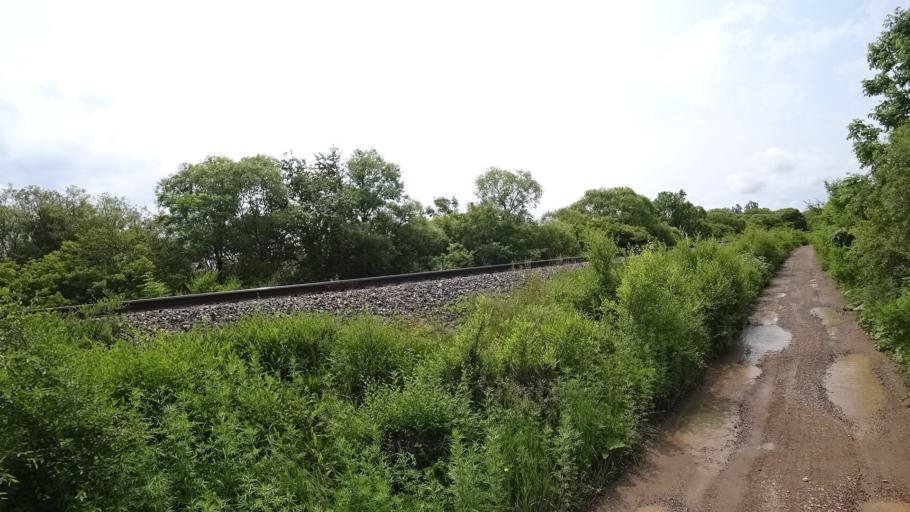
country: RU
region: Primorskiy
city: Novosysoyevka
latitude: 44.2494
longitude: 133.3730
